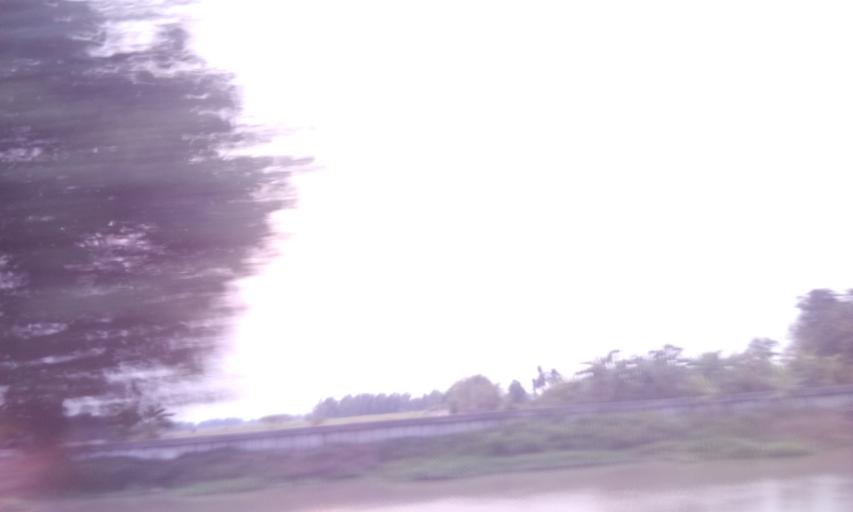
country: TH
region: Bangkok
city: Nong Chok
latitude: 13.9384
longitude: 100.8944
